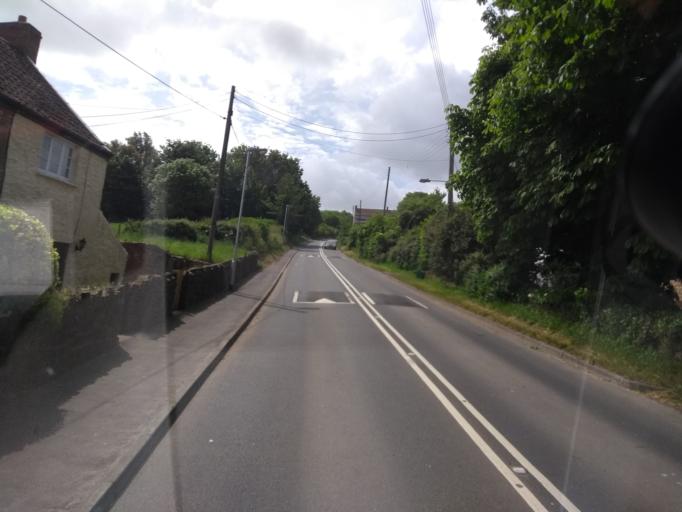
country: GB
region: England
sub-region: Somerset
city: Bridgwater
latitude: 51.1565
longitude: -3.0647
